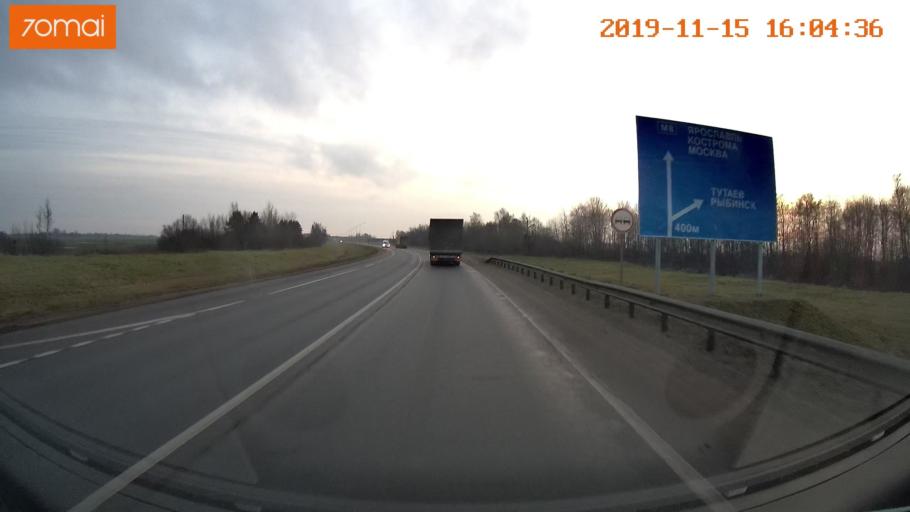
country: RU
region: Jaroslavl
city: Yaroslavl
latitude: 57.7462
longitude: 39.8996
